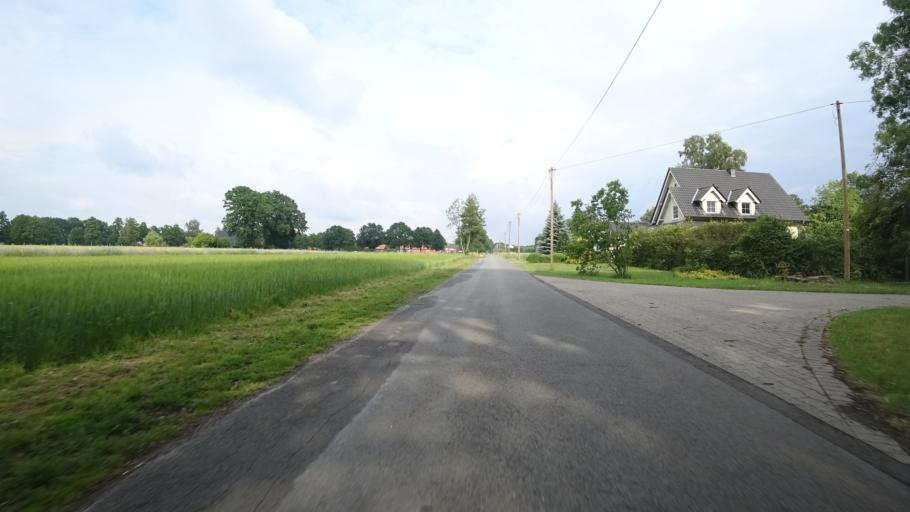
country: DE
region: North Rhine-Westphalia
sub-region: Regierungsbezirk Detmold
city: Guetersloh
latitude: 51.9470
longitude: 8.3727
